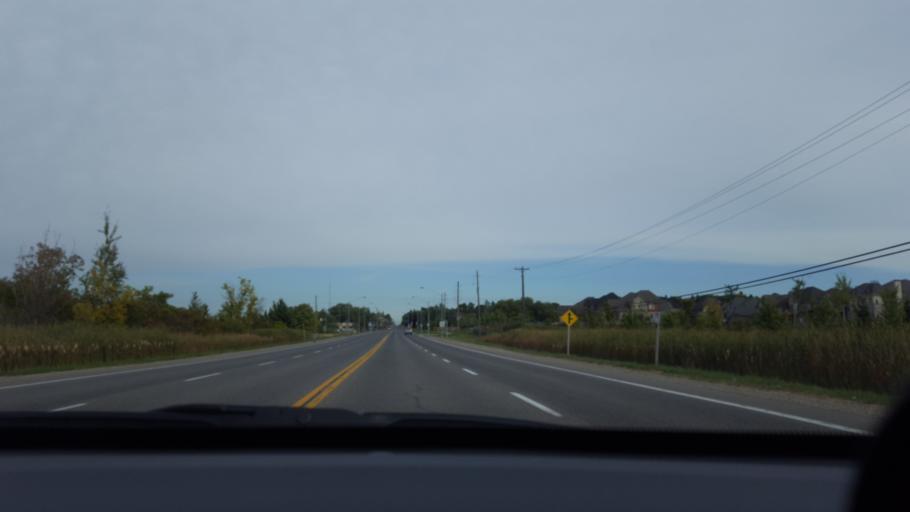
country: CA
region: Ontario
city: Vaughan
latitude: 43.9171
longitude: -79.5251
